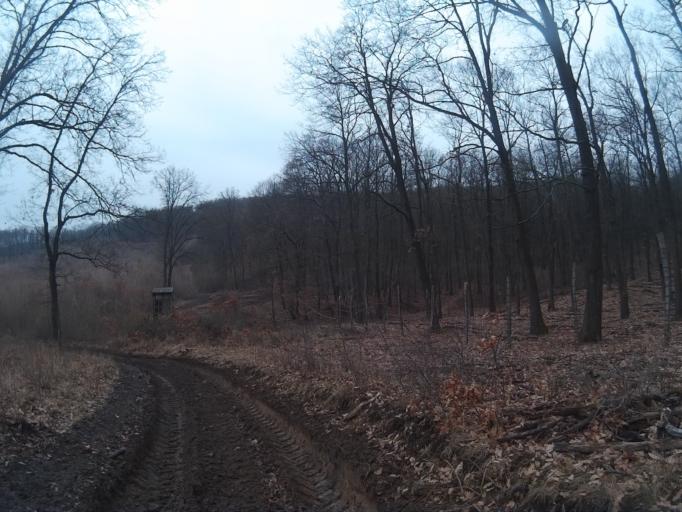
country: HU
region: Komarom-Esztergom
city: Tarjan
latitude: 47.5683
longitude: 18.5478
